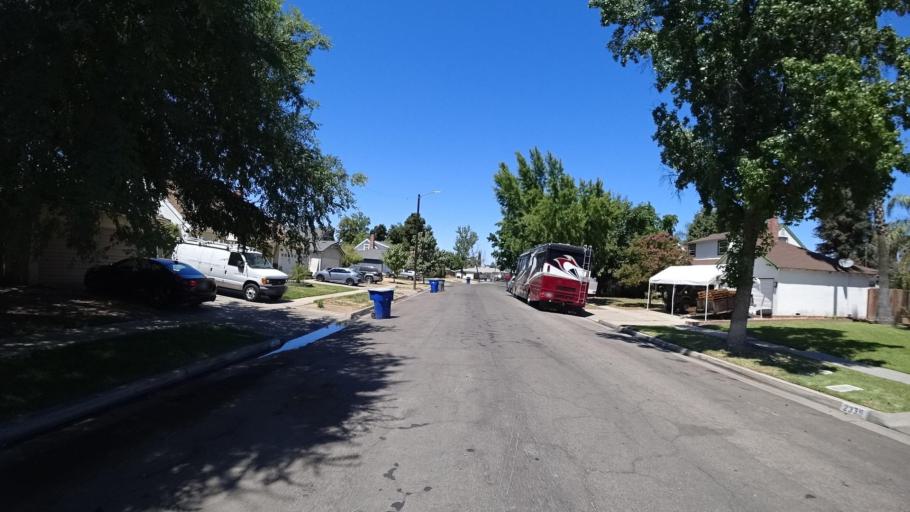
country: US
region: California
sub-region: Fresno County
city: Fresno
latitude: 36.8064
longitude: -119.7825
